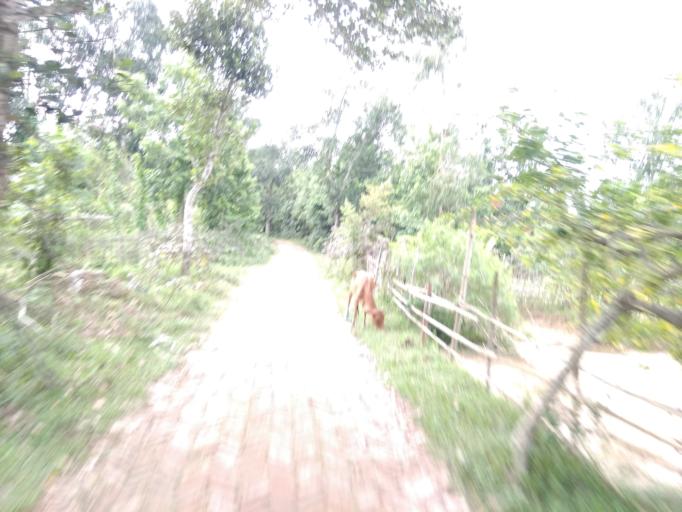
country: BD
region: Chittagong
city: Manikchari
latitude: 22.9290
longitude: 91.9127
